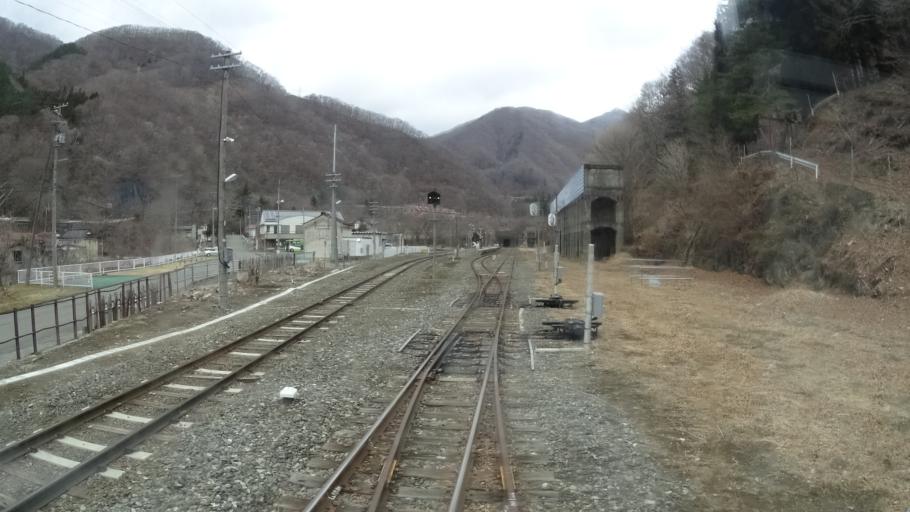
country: JP
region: Iwate
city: Kamaishi
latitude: 39.2794
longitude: 141.7192
